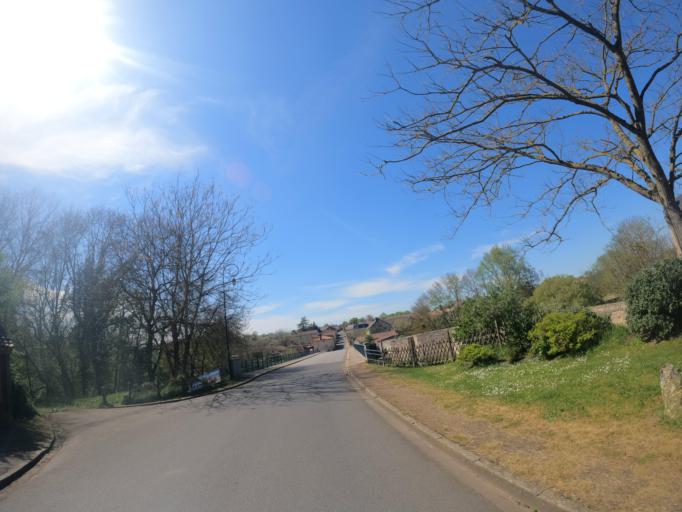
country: FR
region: Poitou-Charentes
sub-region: Departement des Deux-Sevres
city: Airvault
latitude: 46.8837
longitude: -0.1393
